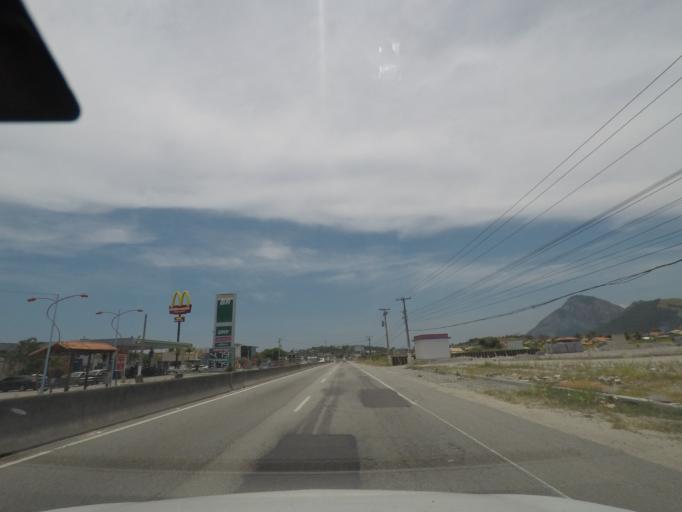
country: BR
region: Rio de Janeiro
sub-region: Marica
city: Marica
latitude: -22.9280
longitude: -42.8689
